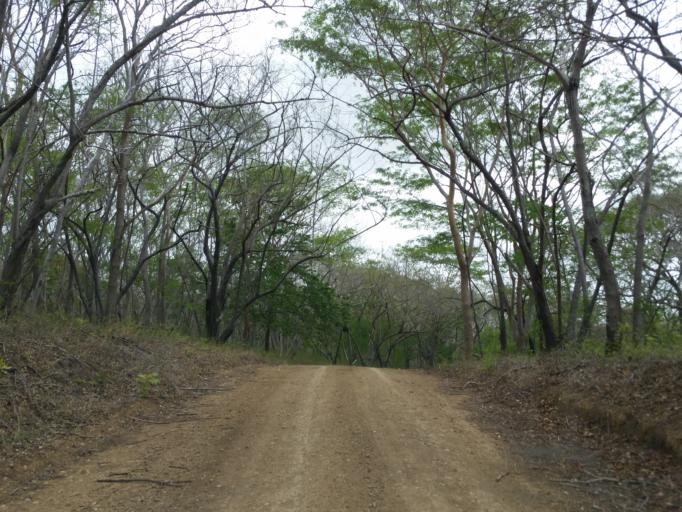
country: NI
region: Rivas
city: Tola
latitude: 11.4184
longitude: -86.0618
